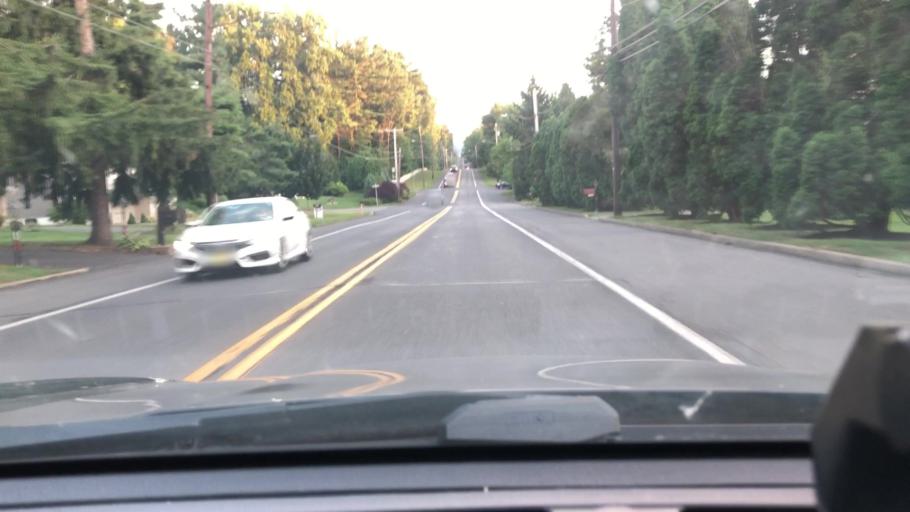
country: US
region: Pennsylvania
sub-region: Northampton County
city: Bethlehem
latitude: 40.6522
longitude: -75.3775
